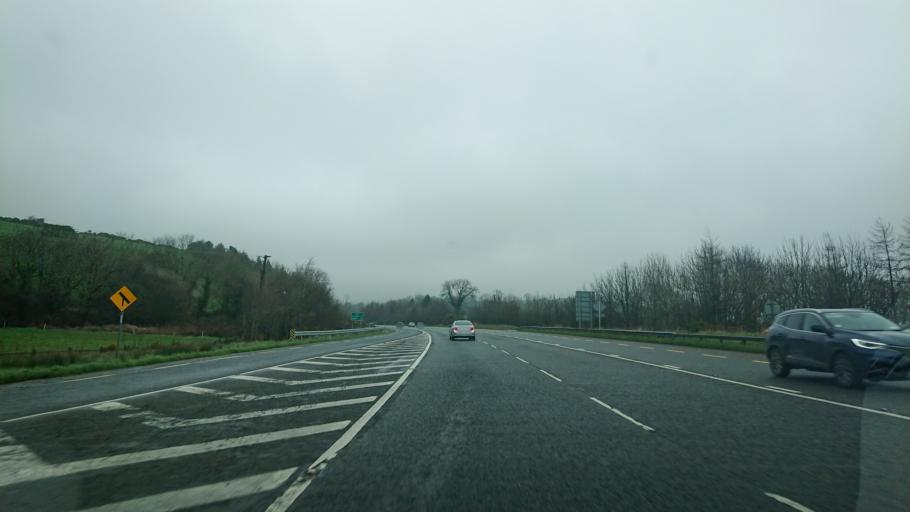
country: IE
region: Munster
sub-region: County Cork
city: Kinsale
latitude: 51.8126
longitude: -8.5374
